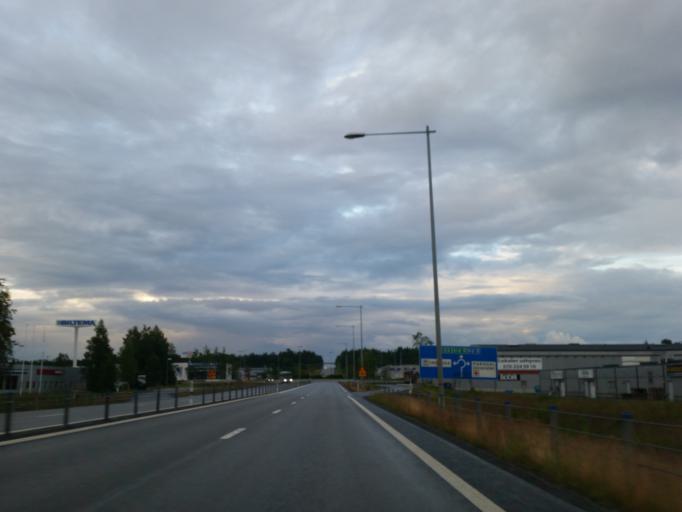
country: SE
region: Vaesterbotten
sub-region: Umea Kommun
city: Ersmark
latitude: 63.8486
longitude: 20.3082
